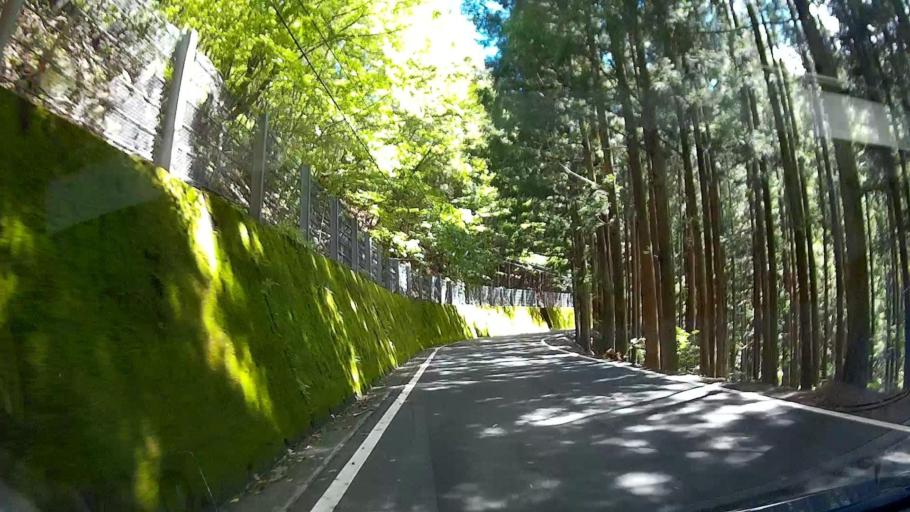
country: JP
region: Shizuoka
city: Shizuoka-shi
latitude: 35.2059
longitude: 138.2331
